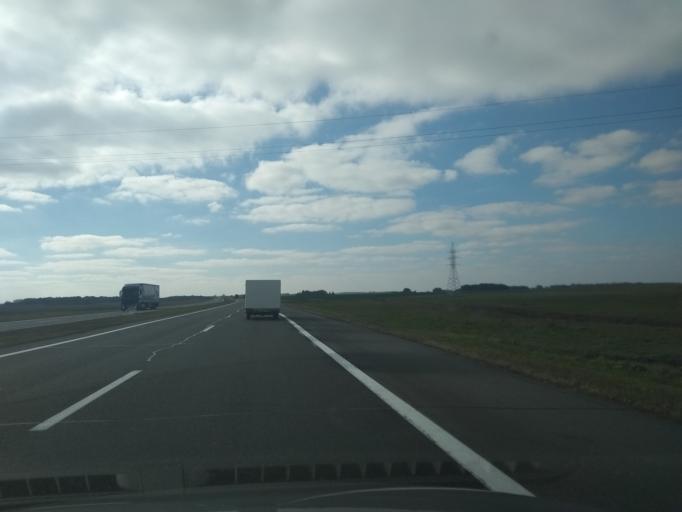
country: BY
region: Brest
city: Haradzishcha
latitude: 53.2329
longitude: 26.1720
